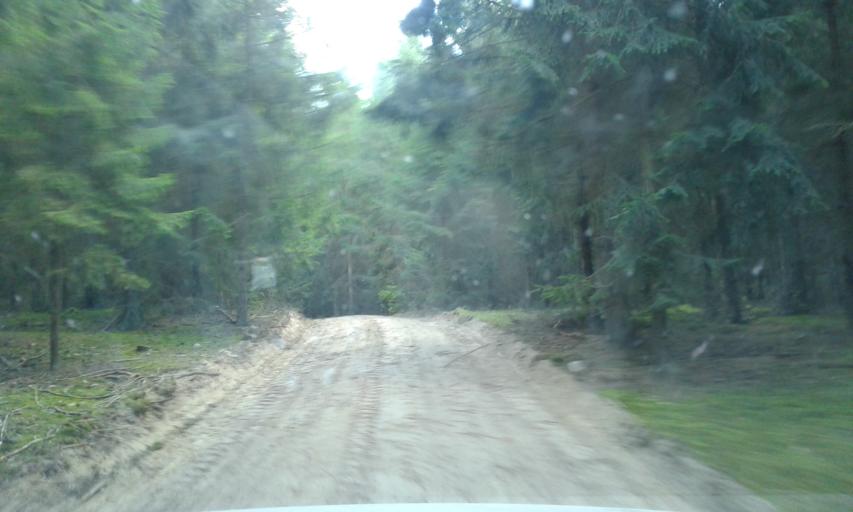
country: PL
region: West Pomeranian Voivodeship
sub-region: Powiat stargardzki
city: Dolice
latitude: 53.2296
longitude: 15.2483
